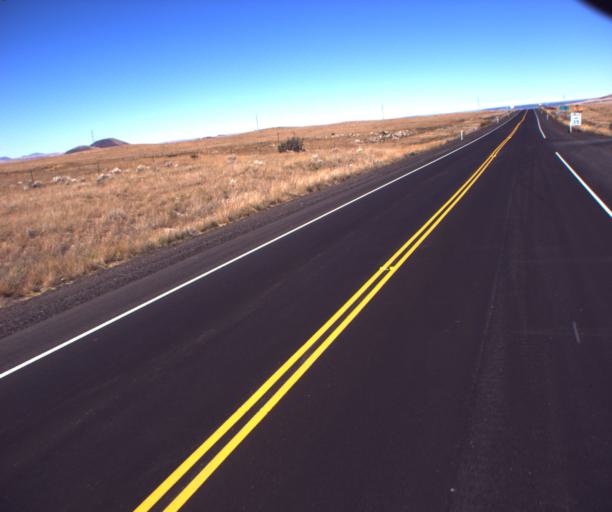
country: US
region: Arizona
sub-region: Apache County
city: Springerville
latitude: 34.1766
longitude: -109.3179
